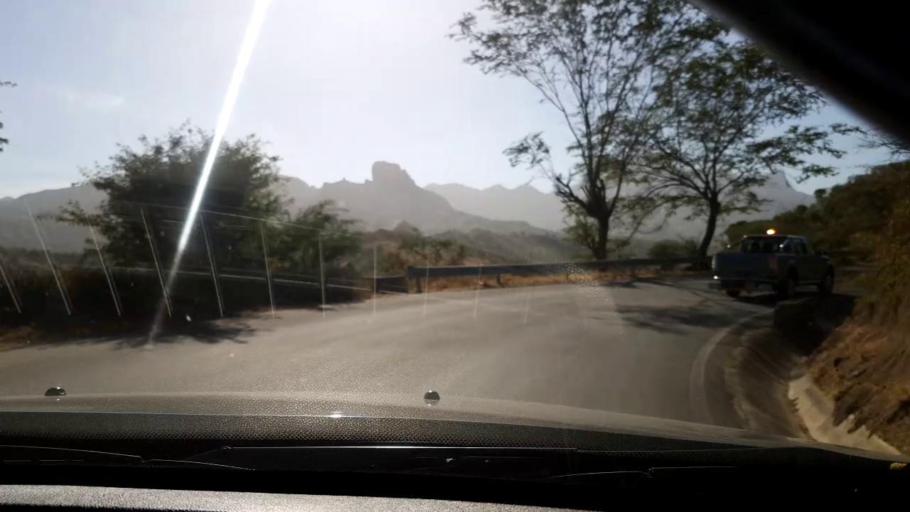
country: CV
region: Sao Lourenco dos Orgaos
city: Joao Teves
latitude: 15.0722
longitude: -23.5660
